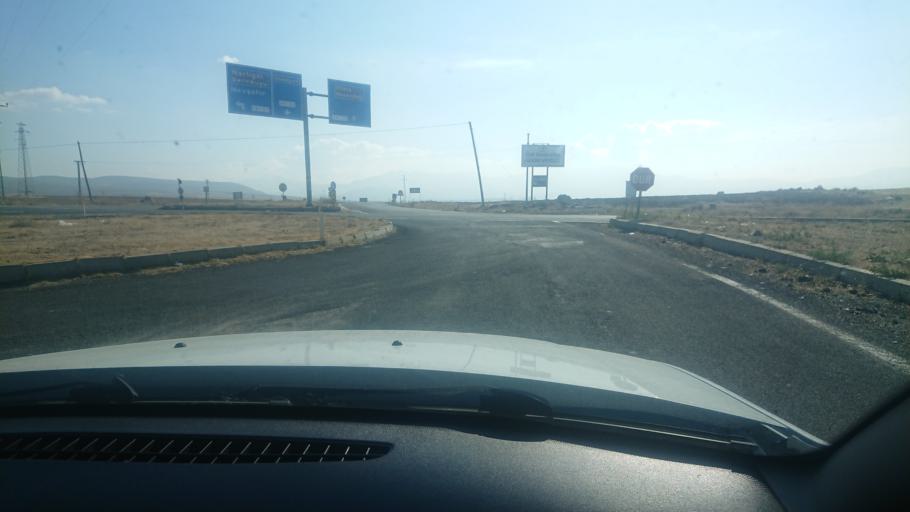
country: TR
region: Aksaray
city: Guzelyurt
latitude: 38.2878
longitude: 34.3211
